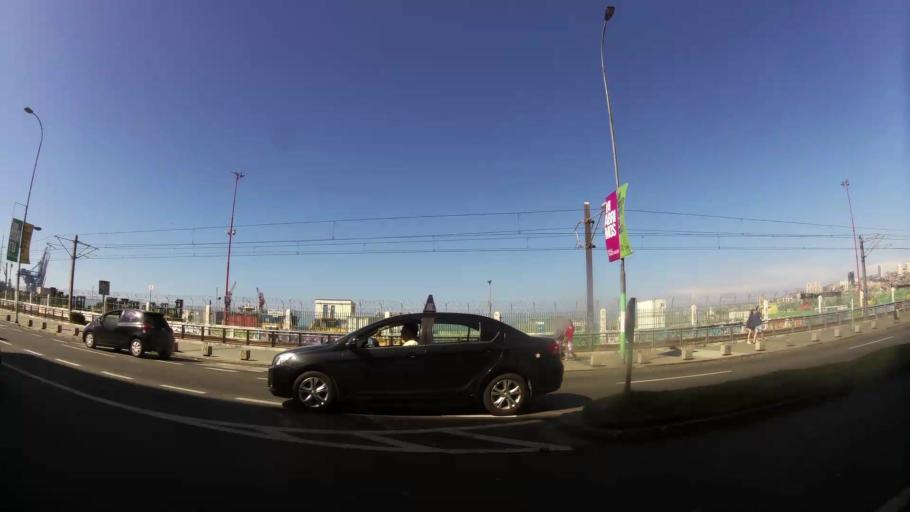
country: CL
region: Valparaiso
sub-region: Provincia de Valparaiso
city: Valparaiso
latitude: -33.0413
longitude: -71.6241
